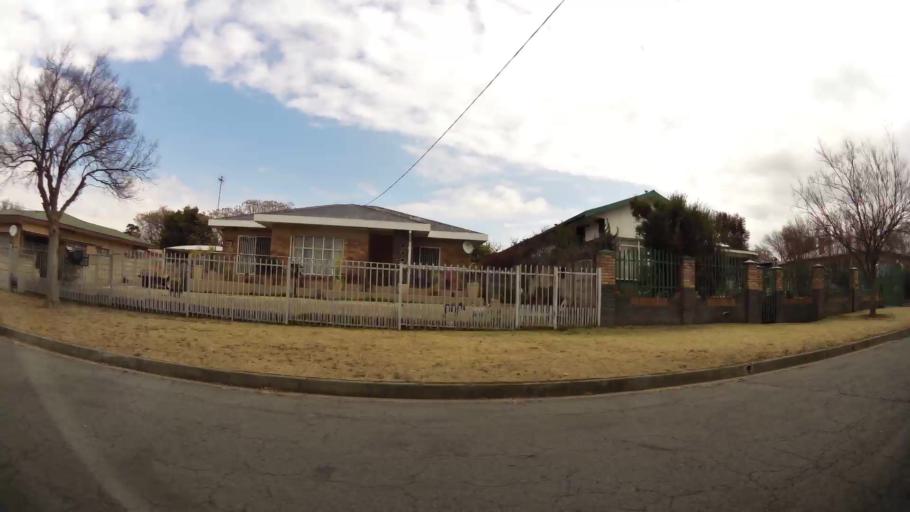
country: ZA
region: Orange Free State
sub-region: Fezile Dabi District Municipality
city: Kroonstad
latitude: -27.6480
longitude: 27.2377
